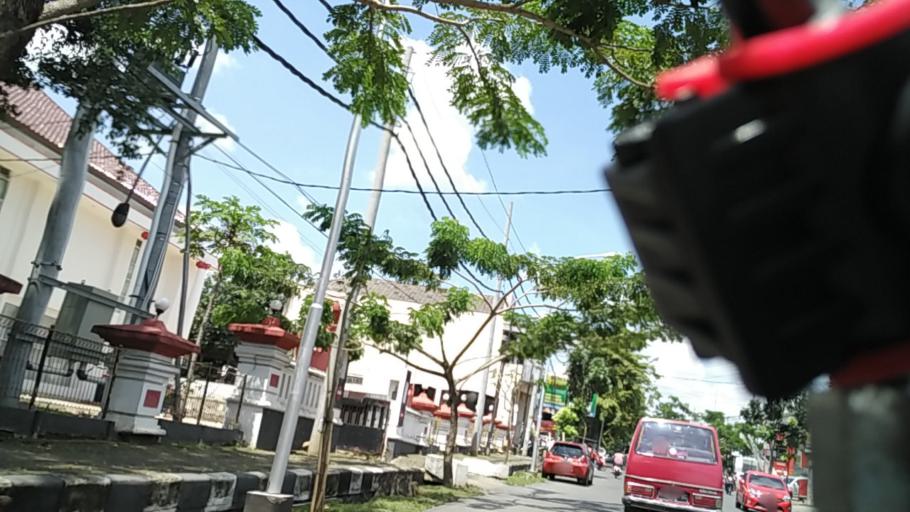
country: ID
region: Central Java
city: Semarang
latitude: -7.0526
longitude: 110.4284
